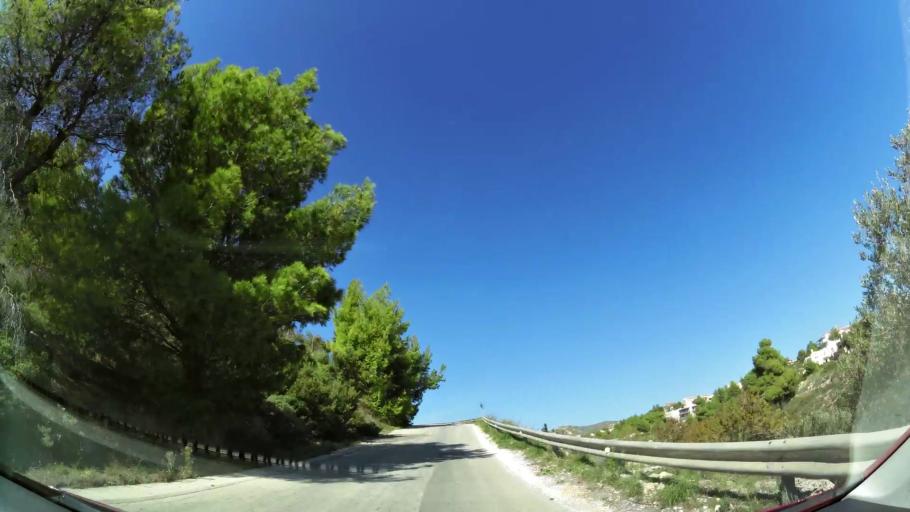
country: GR
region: Attica
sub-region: Nomarchia Anatolikis Attikis
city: Dioni
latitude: 38.0204
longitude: 23.9269
